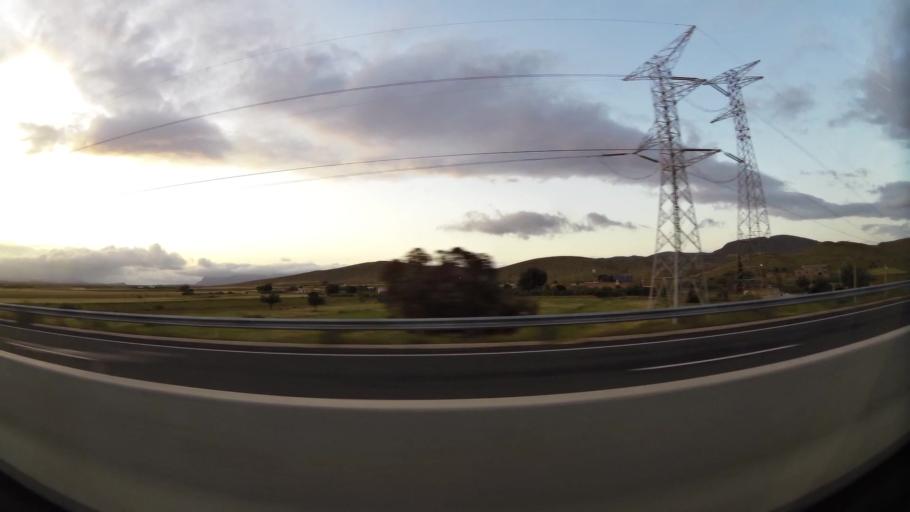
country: MA
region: Oriental
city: El Aioun
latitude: 34.5951
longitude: -2.6756
